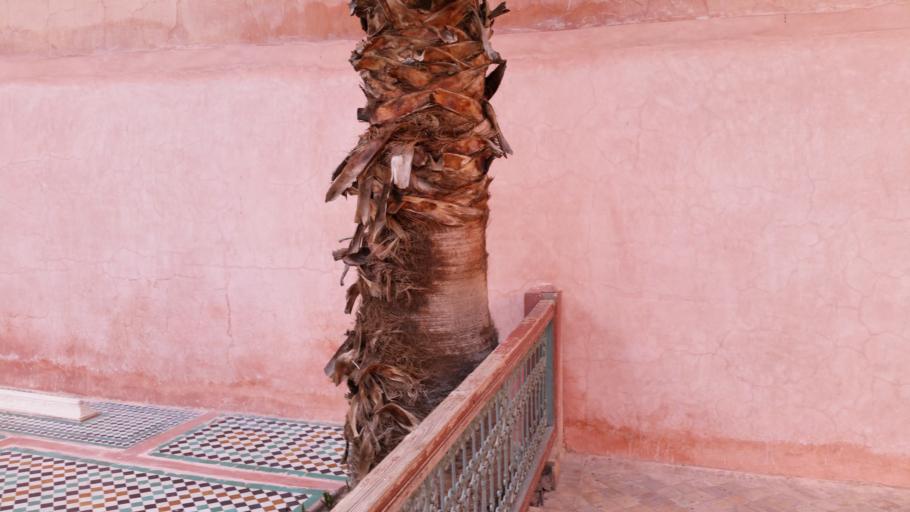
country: MA
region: Marrakech-Tensift-Al Haouz
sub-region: Marrakech
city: Marrakesh
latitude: 31.6173
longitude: -7.9885
